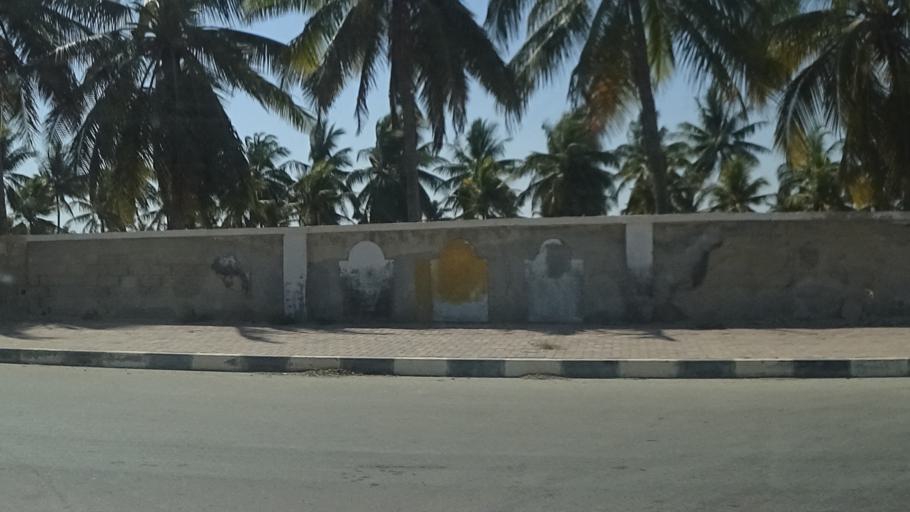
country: OM
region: Zufar
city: Salalah
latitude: 17.0322
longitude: 54.1721
